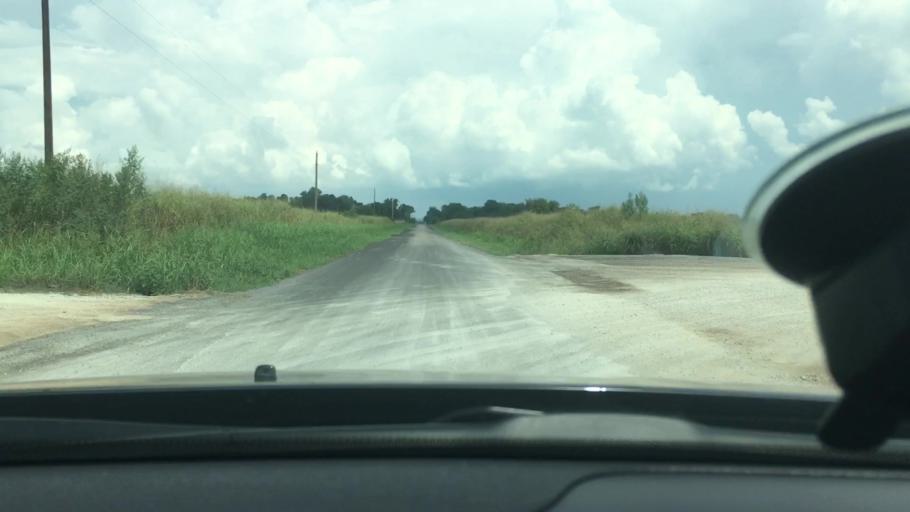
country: US
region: Oklahoma
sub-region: Carter County
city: Dickson
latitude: 34.2089
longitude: -96.8982
